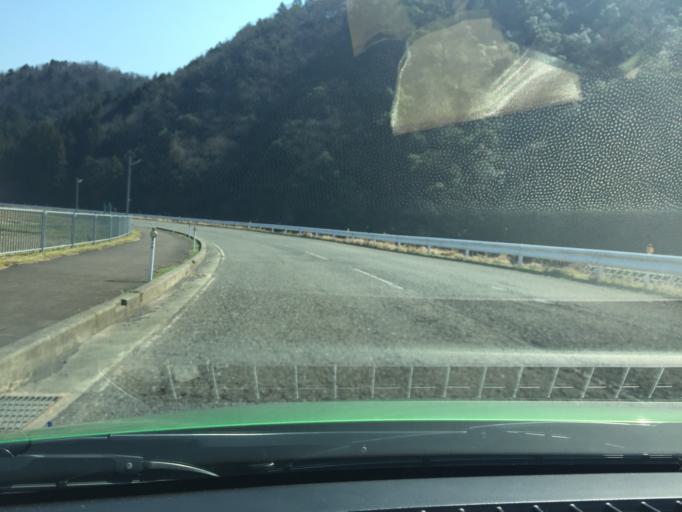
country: JP
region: Fukui
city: Obama
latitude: 35.3998
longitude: 135.6268
